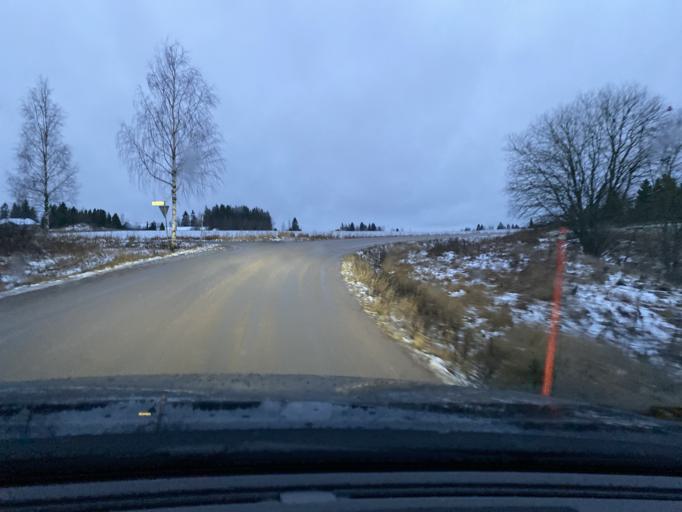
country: FI
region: Pirkanmaa
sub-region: Lounais-Pirkanmaa
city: Punkalaidun
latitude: 61.1212
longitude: 23.0281
